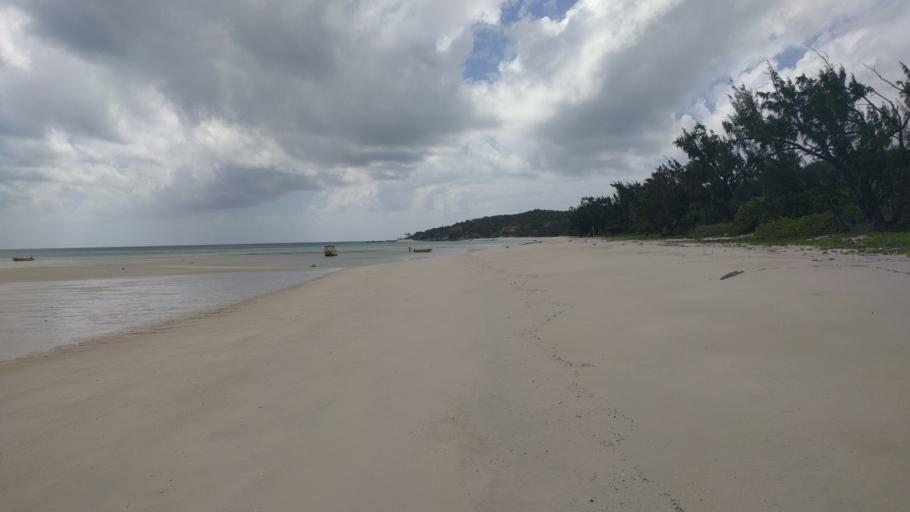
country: AU
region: Queensland
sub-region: Cook
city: Cooktown
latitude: -14.6807
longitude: 145.4479
